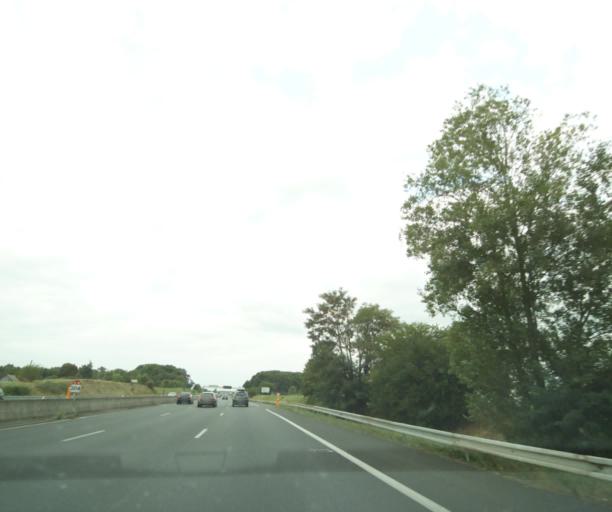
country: FR
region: Centre
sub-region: Departement d'Indre-et-Loire
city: Rochecorbon
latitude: 47.4138
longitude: 0.7294
